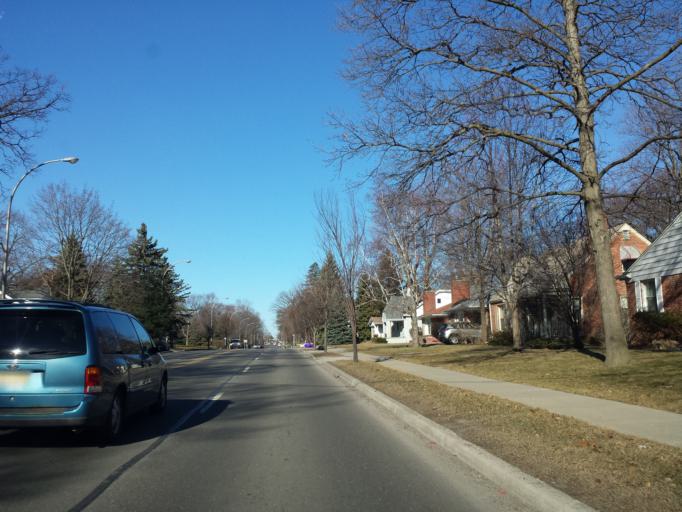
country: US
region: Michigan
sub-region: Oakland County
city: Berkley
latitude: 42.5039
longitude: -83.1618
